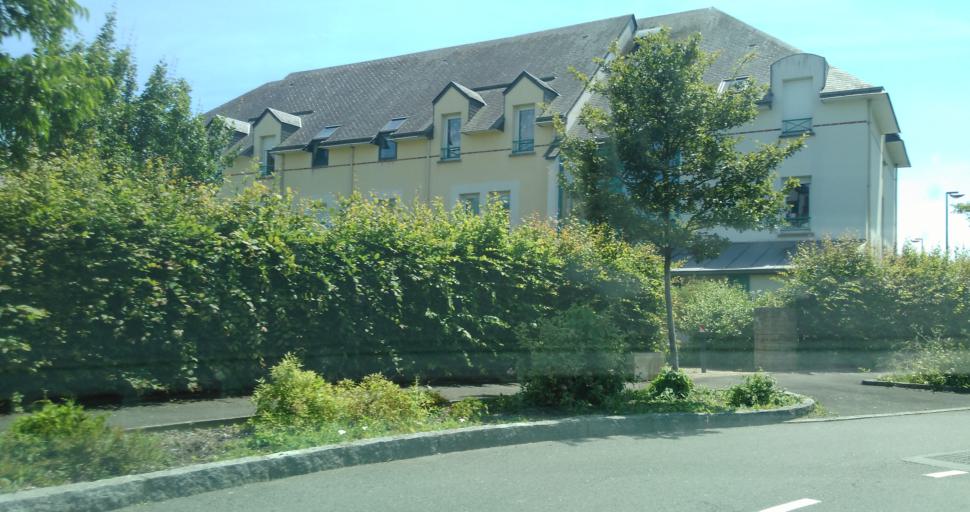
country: FR
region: Brittany
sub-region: Departement d'Ille-et-Vilaine
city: Chantepie
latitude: 48.0924
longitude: -1.6079
